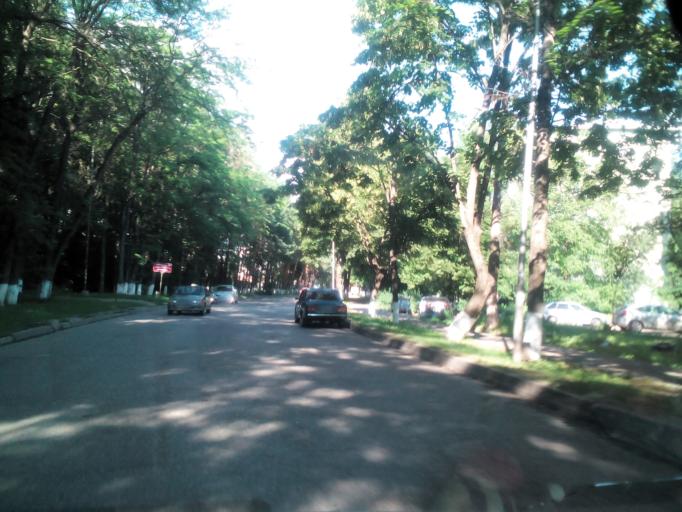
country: RU
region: Stavropol'skiy
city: Pyatigorsk
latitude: 44.0613
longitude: 43.0544
